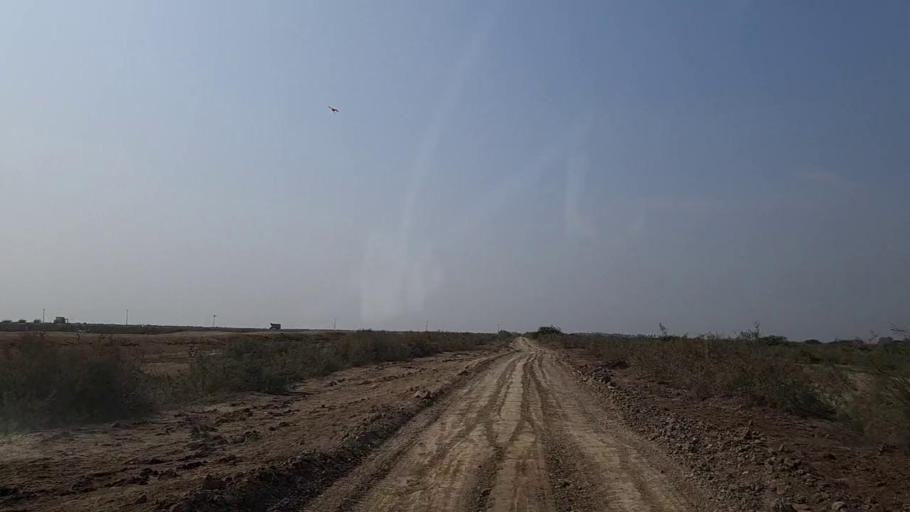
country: PK
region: Sindh
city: Gharo
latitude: 24.6735
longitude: 67.7081
